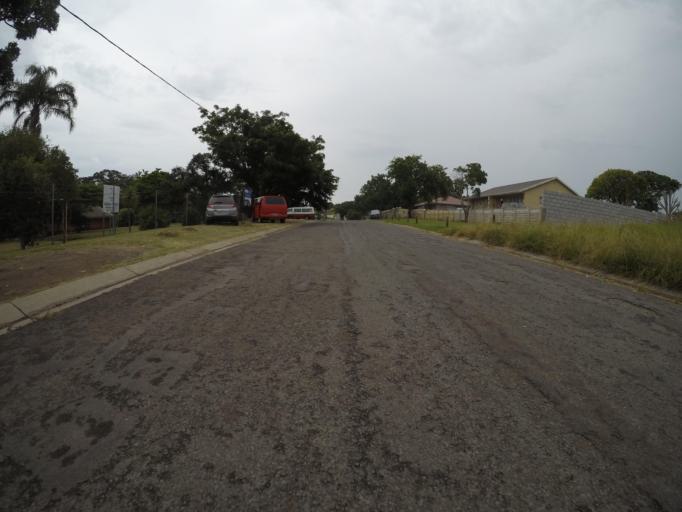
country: ZA
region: Eastern Cape
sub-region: Buffalo City Metropolitan Municipality
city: East London
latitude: -32.9677
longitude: 27.8349
